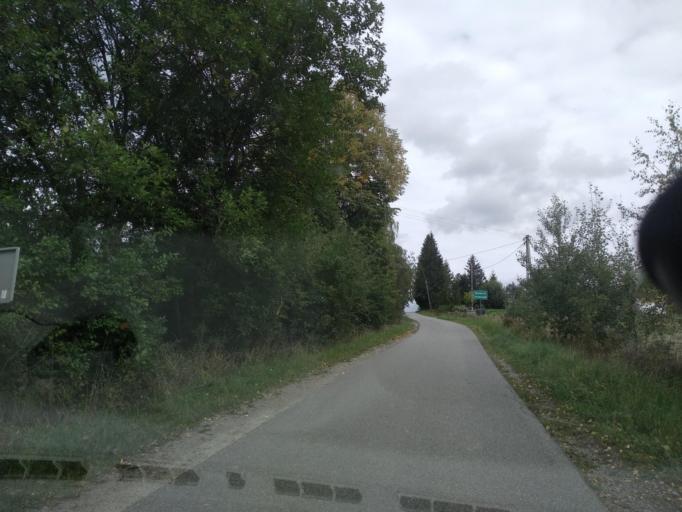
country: PL
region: Lesser Poland Voivodeship
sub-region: Powiat gorlicki
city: Uscie Gorlickie
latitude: 49.5376
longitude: 21.1793
